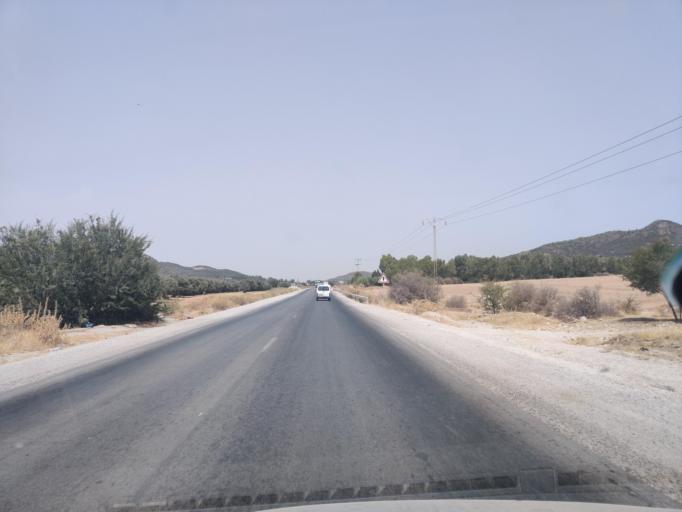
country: TN
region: Tunis
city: Hammam-Lif
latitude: 36.6267
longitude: 10.3984
